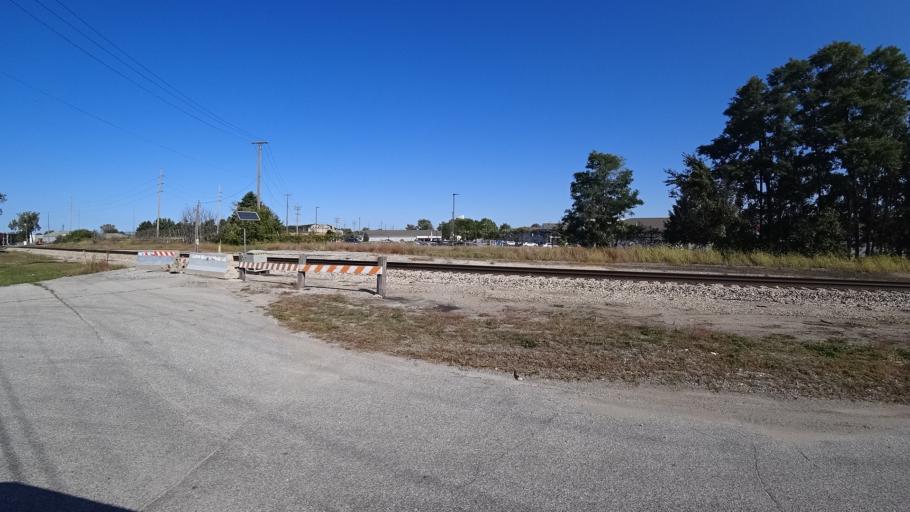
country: US
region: Indiana
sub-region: LaPorte County
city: Michigan City
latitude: 41.7159
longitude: -86.9086
